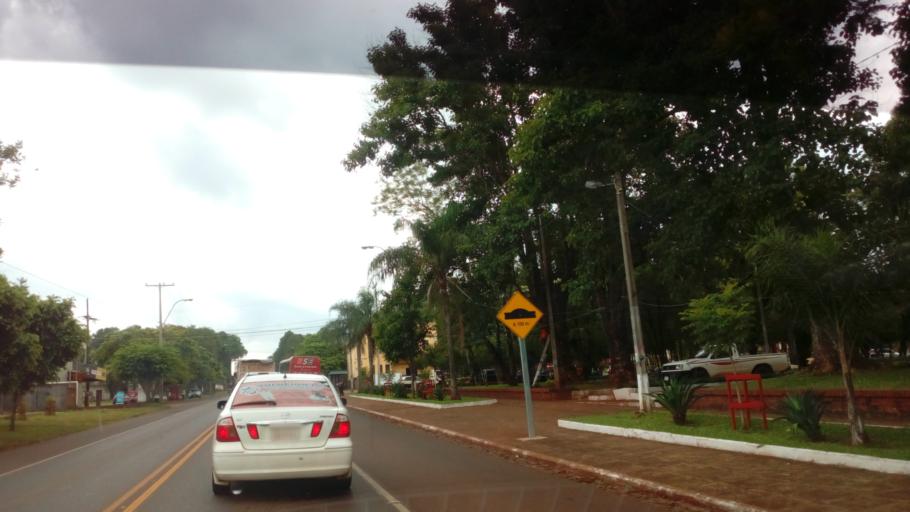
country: PY
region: Itapua
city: Obligado
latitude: -27.0830
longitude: -55.6487
